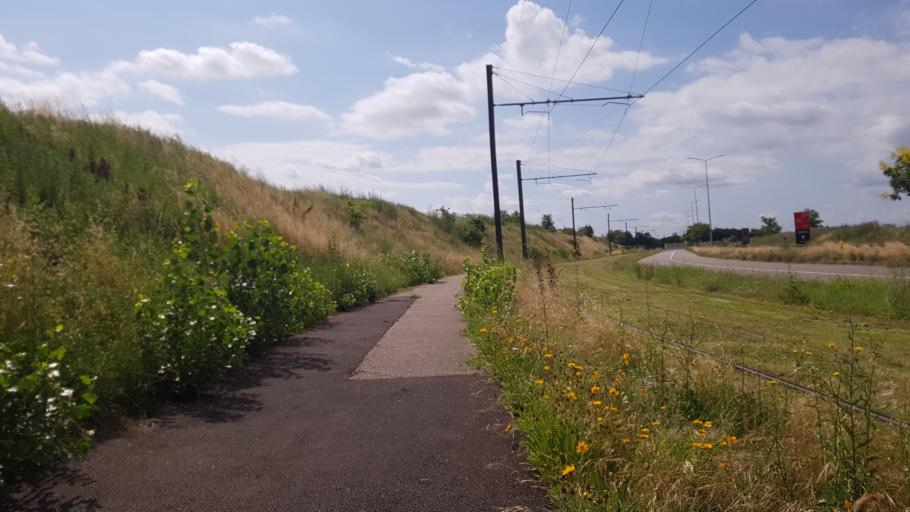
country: FR
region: Rhone-Alpes
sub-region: Departement du Rhone
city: Chassieu
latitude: 45.7376
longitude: 4.9450
